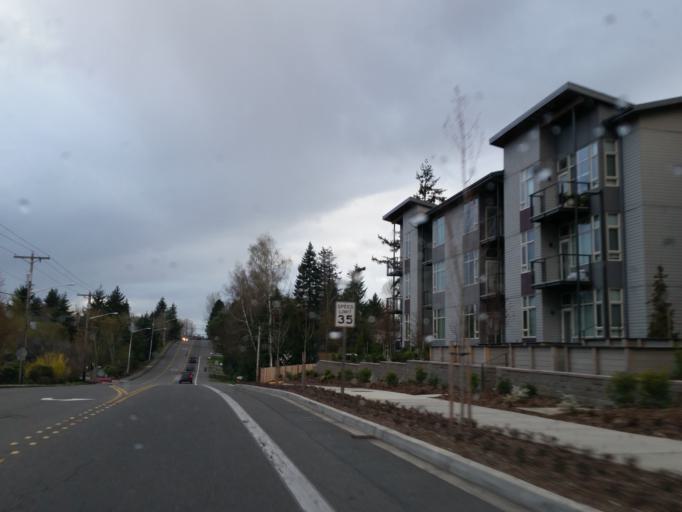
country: US
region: Washington
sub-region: Snohomish County
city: Alderwood Manor
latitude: 47.8137
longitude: -122.2791
